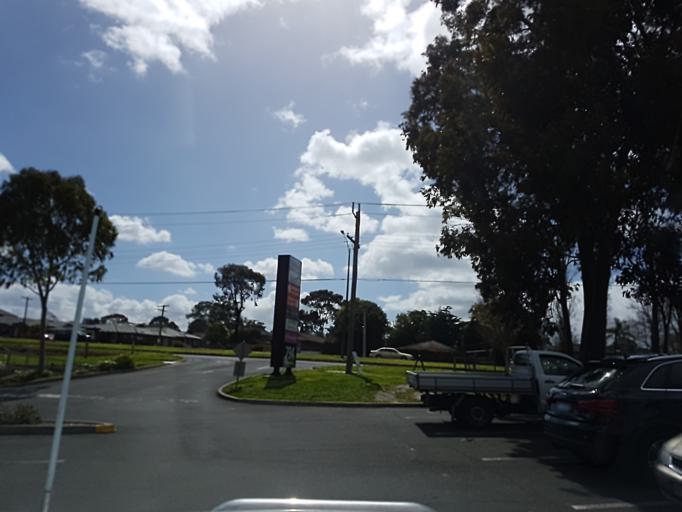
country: AU
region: Victoria
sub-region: Knox
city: Boronia
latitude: -37.8819
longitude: 145.2731
